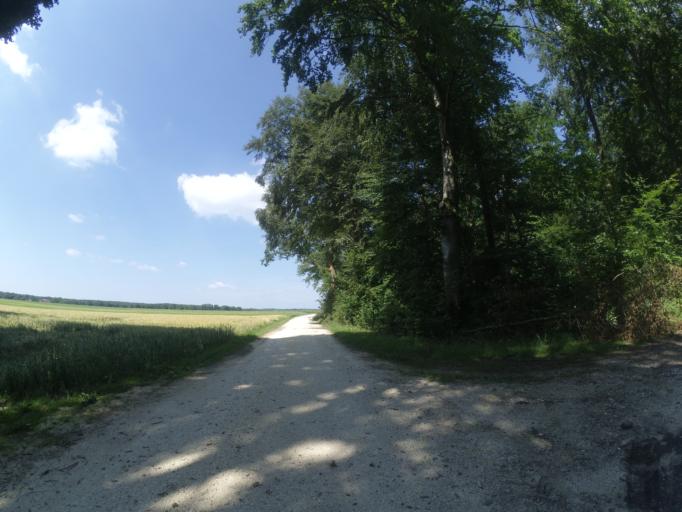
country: DE
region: Baden-Wuerttemberg
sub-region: Tuebingen Region
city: Dornstadt
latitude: 48.4551
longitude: 9.8716
